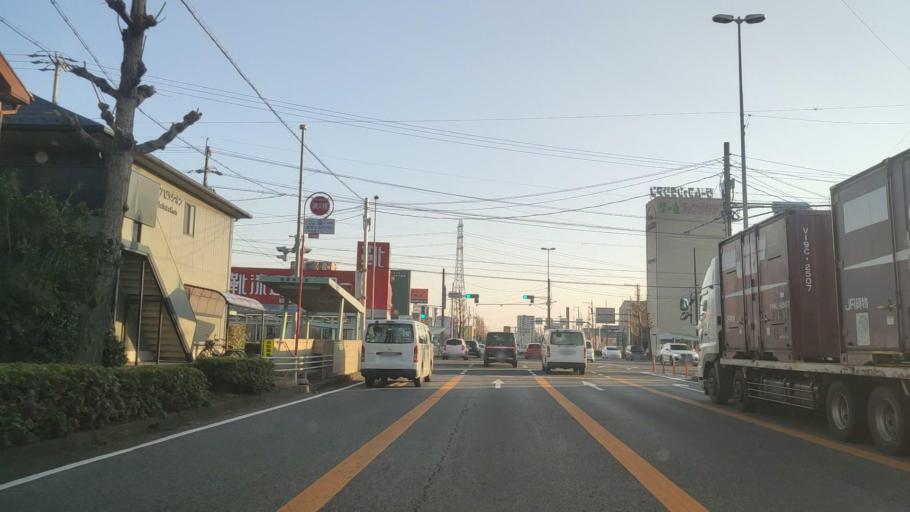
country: JP
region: Gifu
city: Gifu-shi
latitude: 35.4126
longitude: 136.7275
